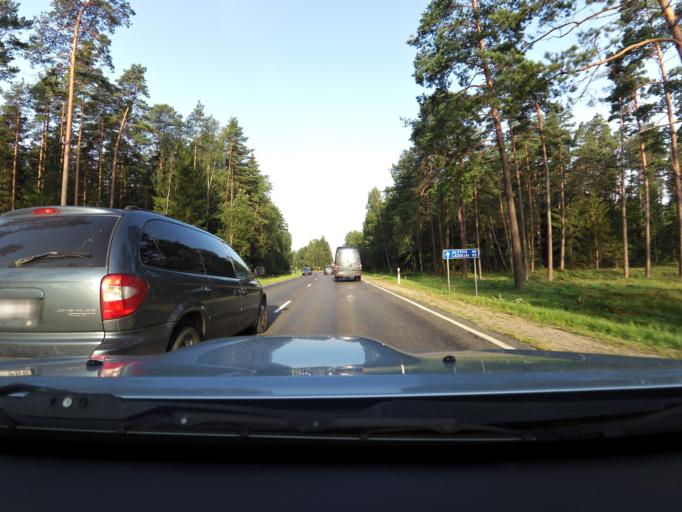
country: LT
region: Alytaus apskritis
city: Varena
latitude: 54.3492
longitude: 24.7033
